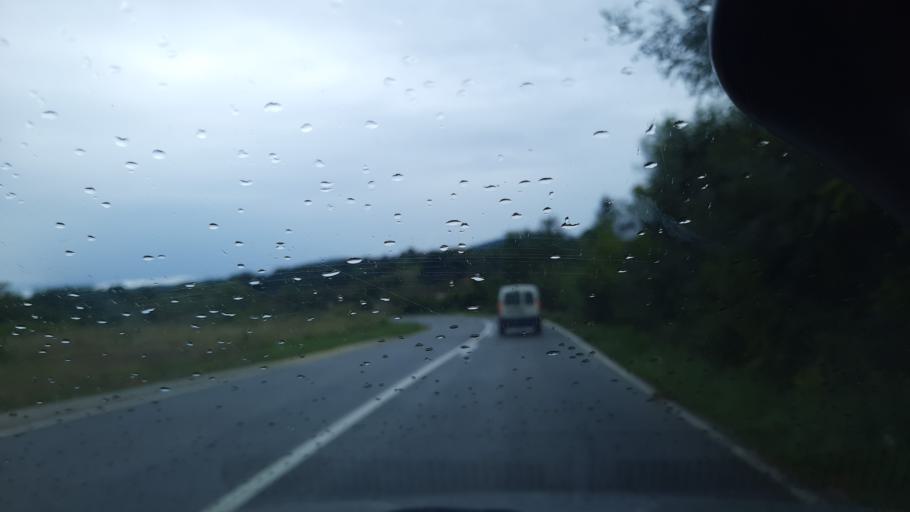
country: RS
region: Central Serbia
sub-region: Raski Okrug
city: Kraljevo
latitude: 43.8042
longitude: 20.7873
